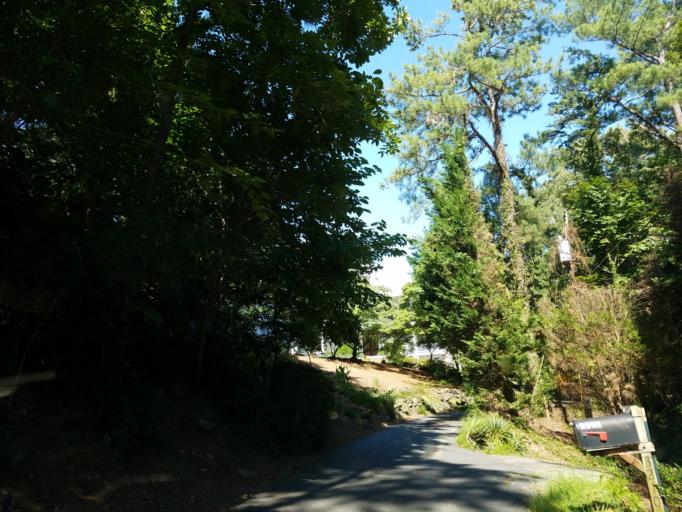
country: US
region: Georgia
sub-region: Cobb County
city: Marietta
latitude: 33.9736
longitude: -84.4585
